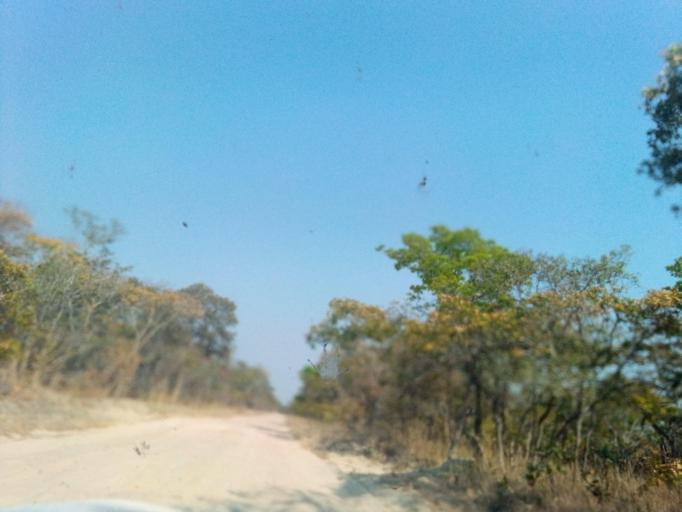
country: ZM
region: Northern
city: Mpika
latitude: -12.2262
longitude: 30.9029
